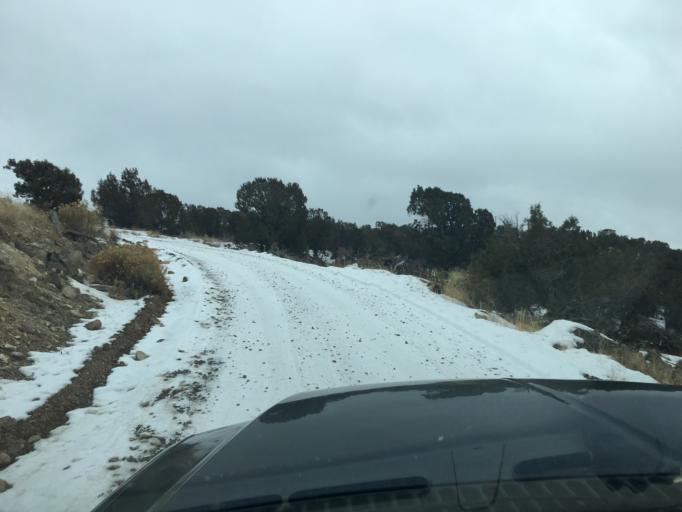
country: US
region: Colorado
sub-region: Garfield County
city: Parachute
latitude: 39.3468
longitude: -108.1699
